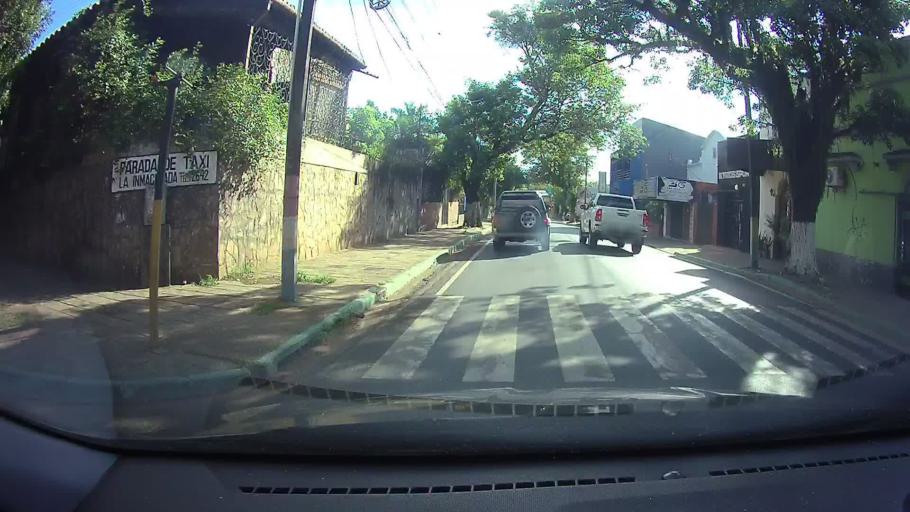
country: PY
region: Cordillera
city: Caacupe
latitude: -25.3837
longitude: -57.1392
